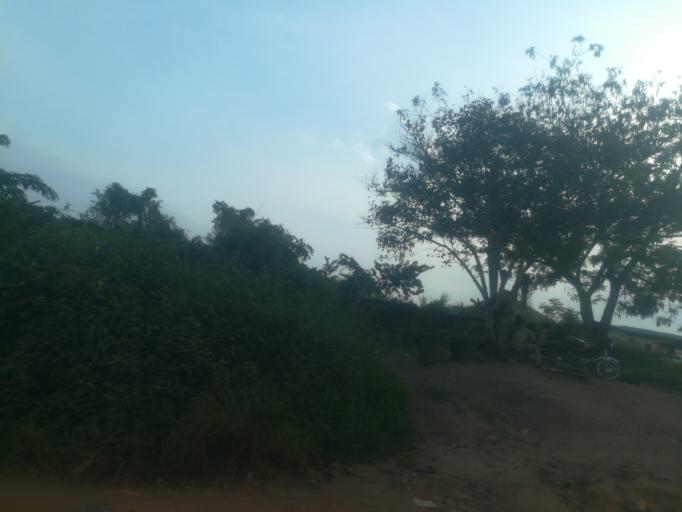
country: NG
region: Ogun
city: Abeokuta
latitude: 7.1399
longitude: 3.2734
